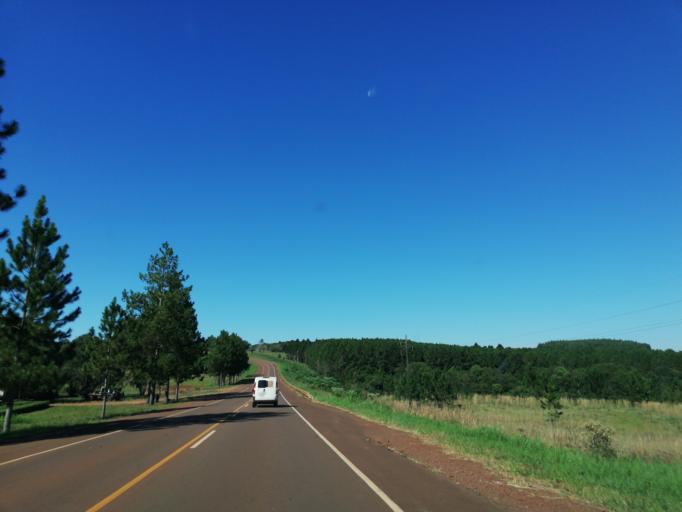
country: AR
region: Misiones
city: Dos de Mayo
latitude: -27.0532
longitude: -54.4299
